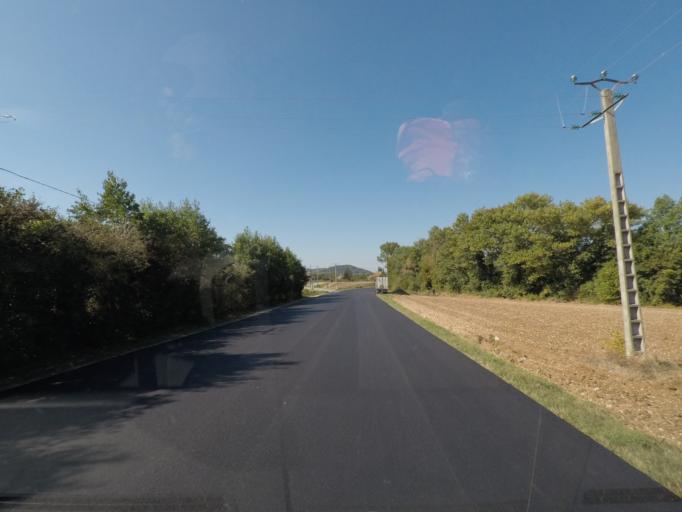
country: FR
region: Rhone-Alpes
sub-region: Departement de la Drome
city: Aouste-sur-Sye
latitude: 44.7038
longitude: 5.1062
